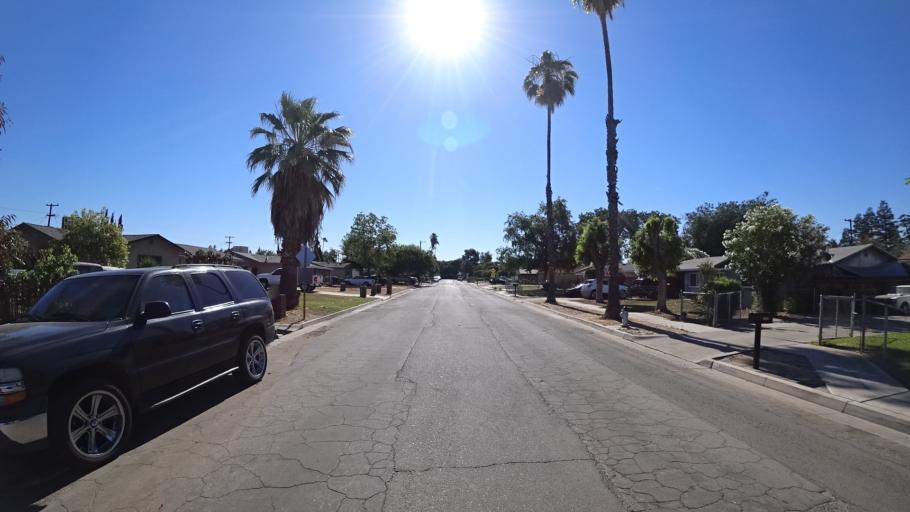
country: US
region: California
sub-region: Fresno County
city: West Park
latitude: 36.7819
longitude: -119.8603
